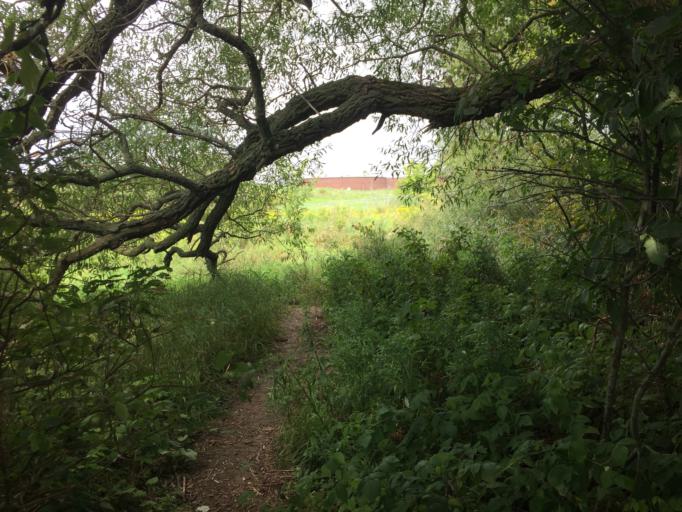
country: CA
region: Ontario
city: Oshawa
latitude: 43.8684
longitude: -78.7526
